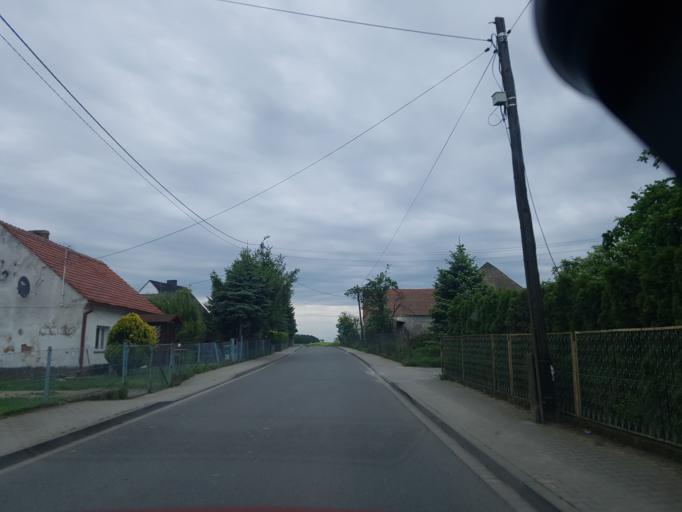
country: PL
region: Lower Silesian Voivodeship
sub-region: Powiat wroclawski
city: Gniechowice
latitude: 50.9850
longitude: 16.7897
